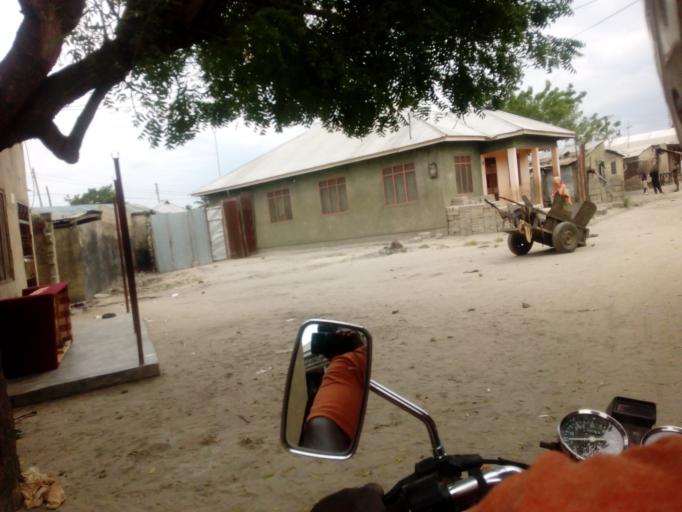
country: TZ
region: Dar es Salaam
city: Dar es Salaam
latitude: -6.8554
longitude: 39.2522
